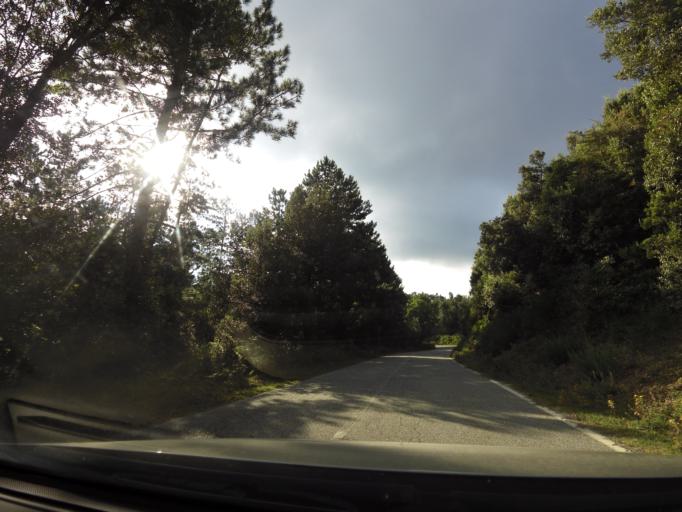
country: IT
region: Calabria
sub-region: Provincia di Vibo-Valentia
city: Nardodipace
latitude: 38.4768
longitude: 16.3891
